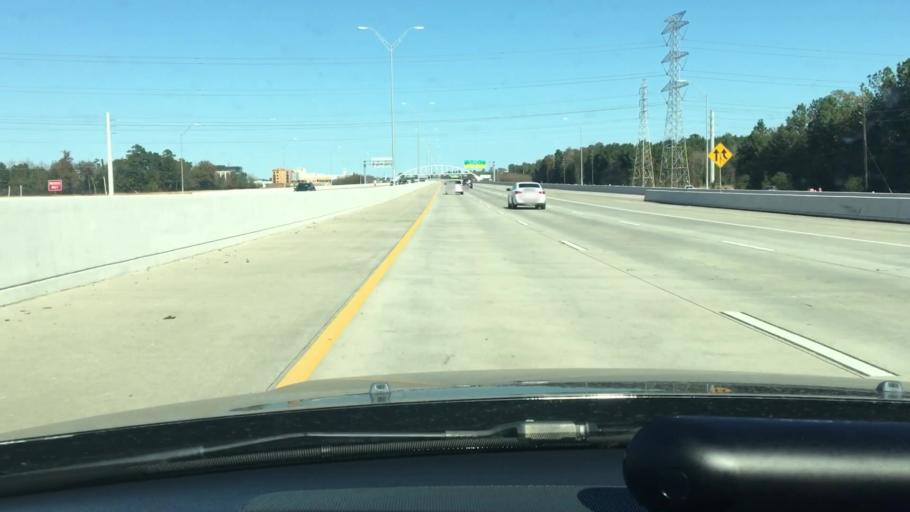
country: US
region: Texas
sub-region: Harris County
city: Sheldon
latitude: 29.9100
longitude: -95.2018
